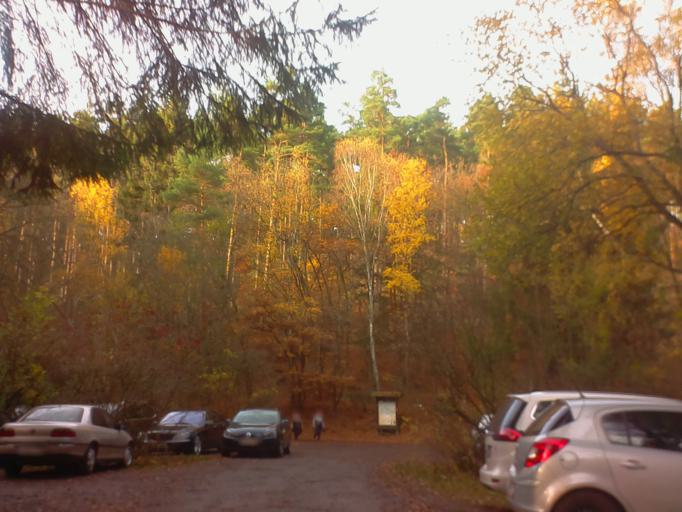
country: DE
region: Rheinland-Pfalz
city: Carlsberg
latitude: 49.4899
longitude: 8.0239
